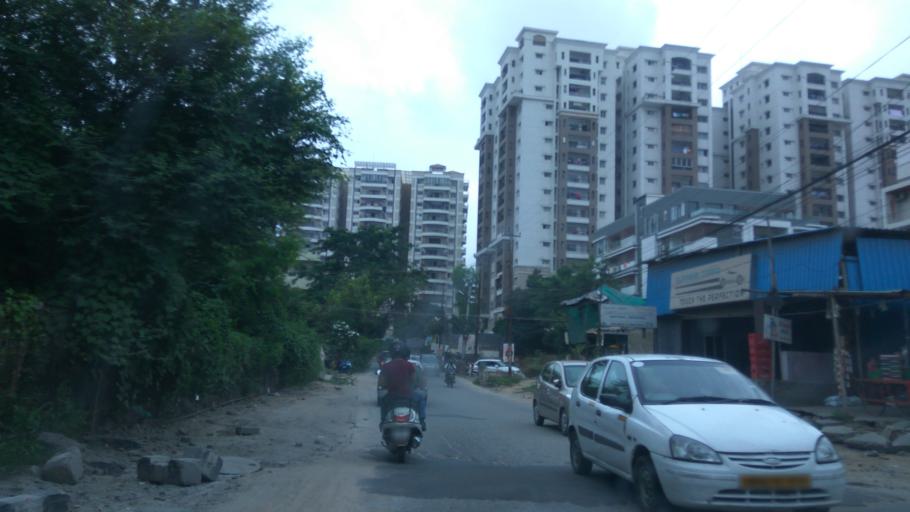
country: IN
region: Telangana
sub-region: Rangareddi
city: Kukatpalli
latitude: 17.4384
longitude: 78.3913
